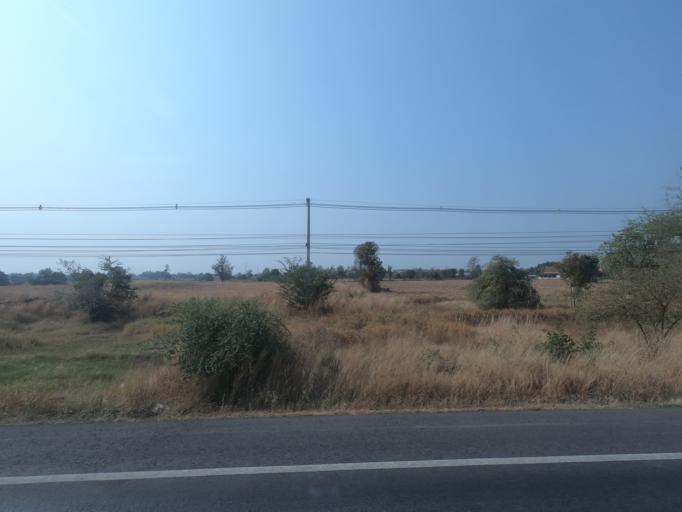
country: TH
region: Khon Kaen
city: Phon
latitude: 15.8822
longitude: 102.6398
